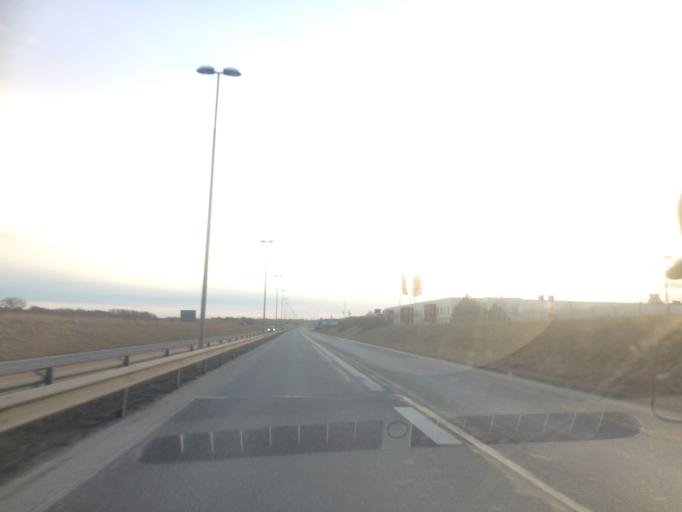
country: SE
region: Vaestra Goetaland
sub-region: Goteborg
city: Torslanda
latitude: 57.7146
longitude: 11.7918
